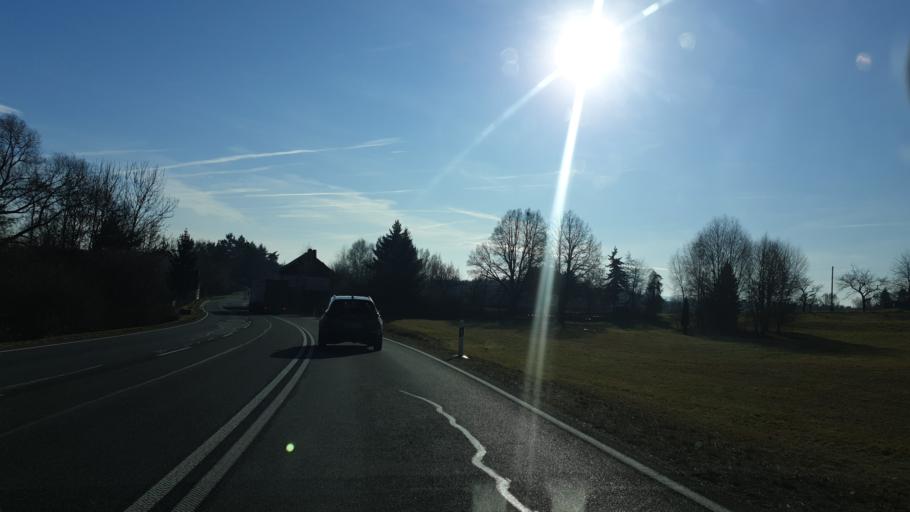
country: DE
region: Saxony
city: Bad Brambach
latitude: 50.1816
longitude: 12.3117
